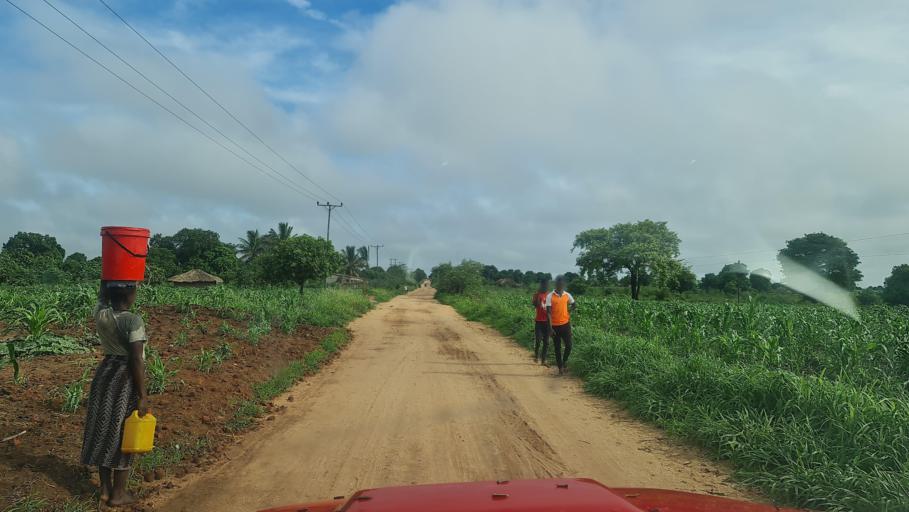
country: MW
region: Southern Region
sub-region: Nsanje District
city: Nsanje
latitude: -17.3105
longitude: 35.5928
